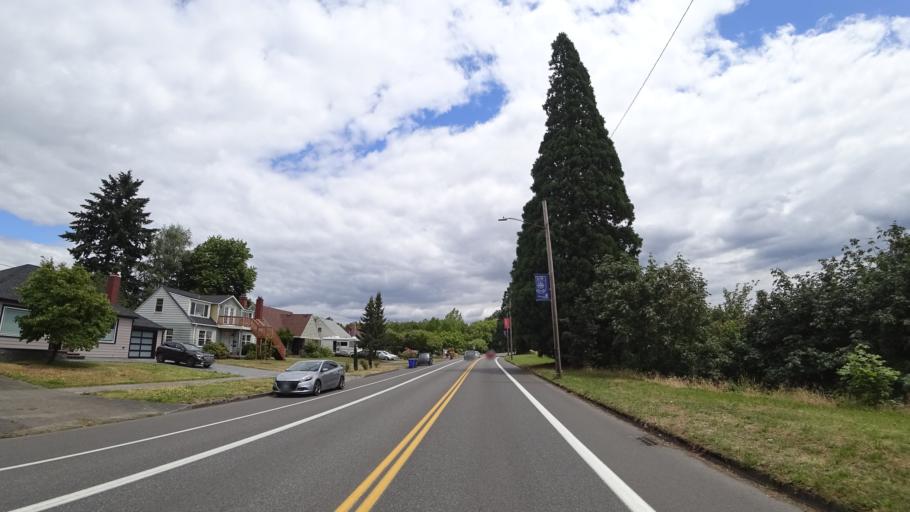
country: US
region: Oregon
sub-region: Multnomah County
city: Portland
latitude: 45.5751
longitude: -122.7156
